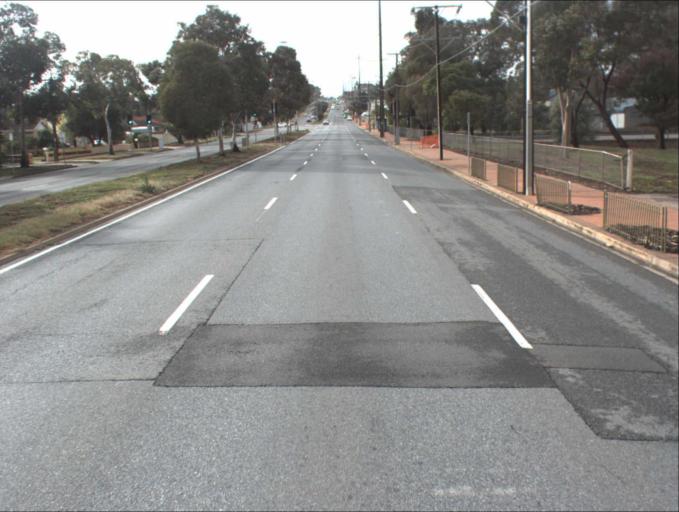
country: AU
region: South Australia
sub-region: Port Adelaide Enfield
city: Enfield
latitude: -34.8480
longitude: 138.6041
